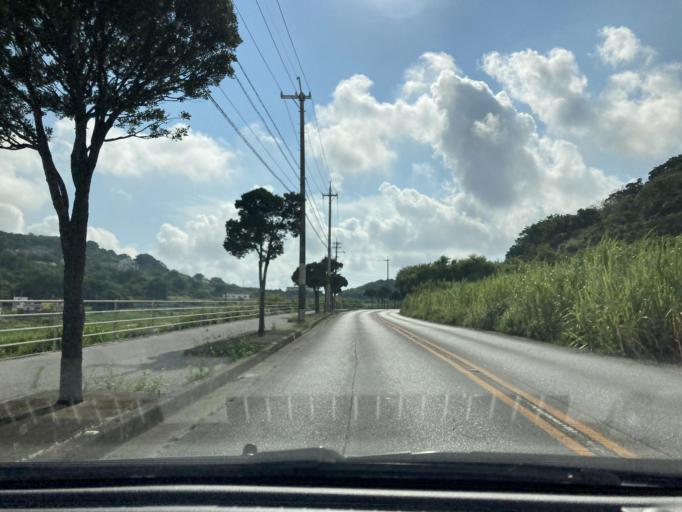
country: JP
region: Okinawa
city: Tomigusuku
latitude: 26.1496
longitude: 127.7539
